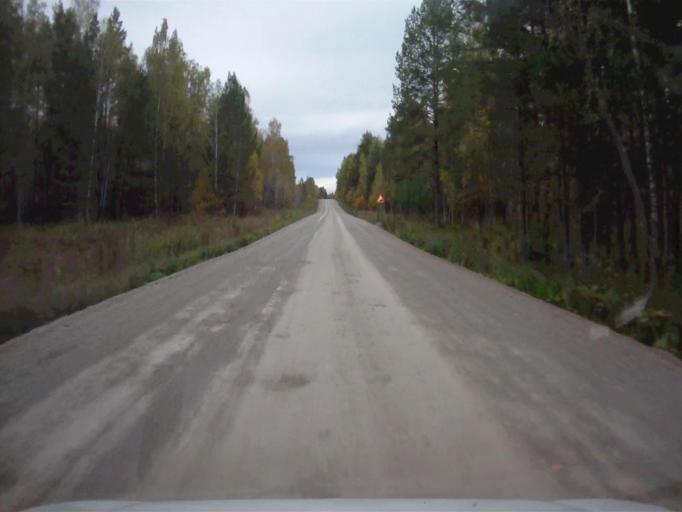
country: RU
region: Chelyabinsk
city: Nyazepetrovsk
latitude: 56.0769
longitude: 59.4257
